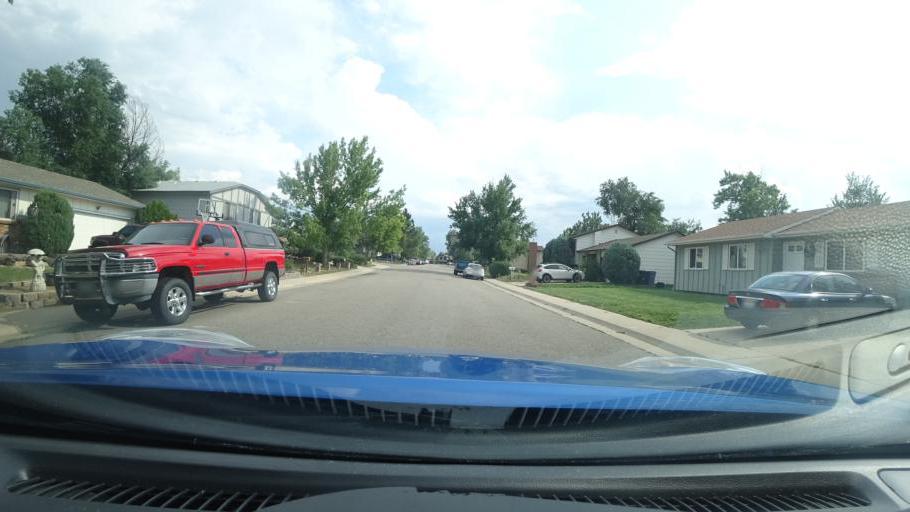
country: US
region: Colorado
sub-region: Adams County
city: Aurora
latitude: 39.6880
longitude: -104.7971
